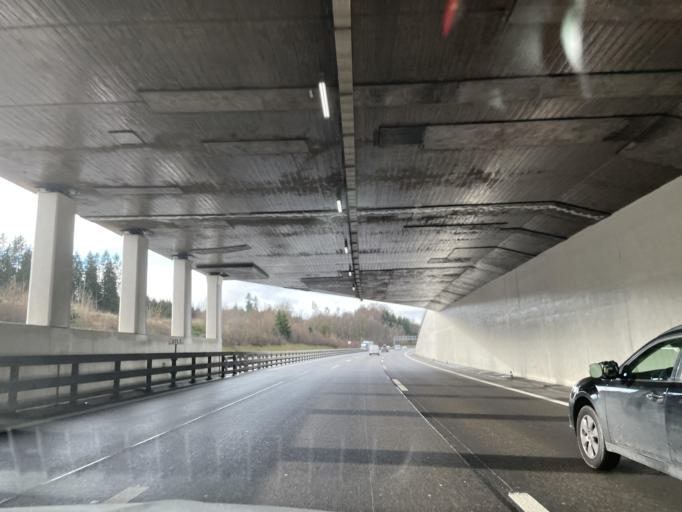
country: CH
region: Zurich
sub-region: Bezirk Pfaeffikon
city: Tagelswangen
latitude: 47.4216
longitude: 8.6647
